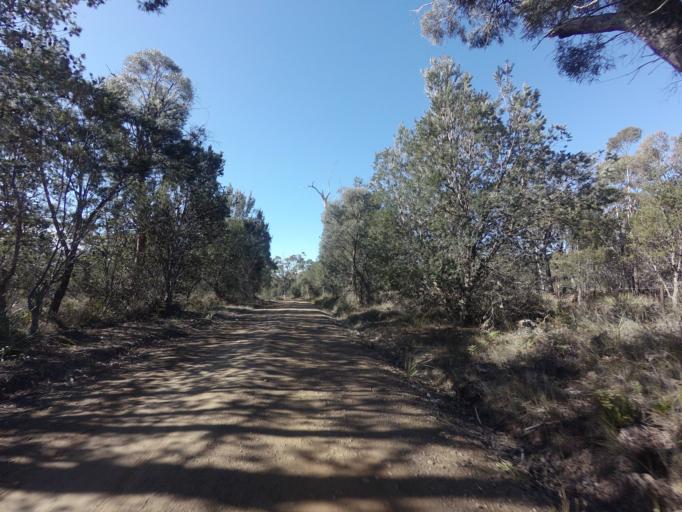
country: AU
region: Tasmania
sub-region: Sorell
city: Sorell
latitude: -42.3511
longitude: 147.9707
